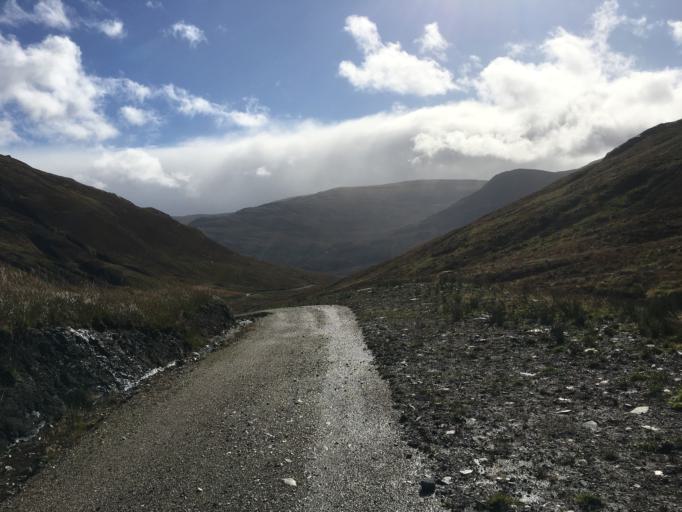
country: GB
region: Scotland
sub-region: Highland
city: Spean Bridge
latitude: 57.3529
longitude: -4.9894
